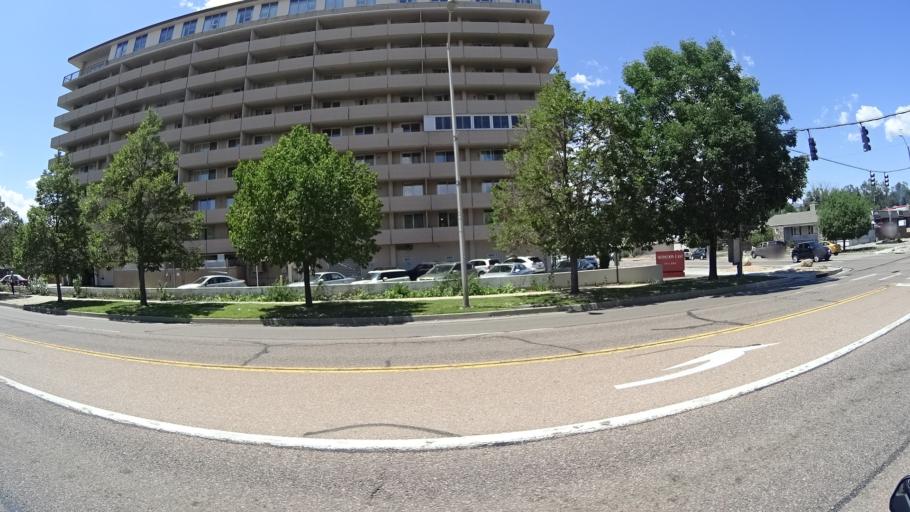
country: US
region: Colorado
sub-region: El Paso County
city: Colorado Springs
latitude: 38.8354
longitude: -104.7945
